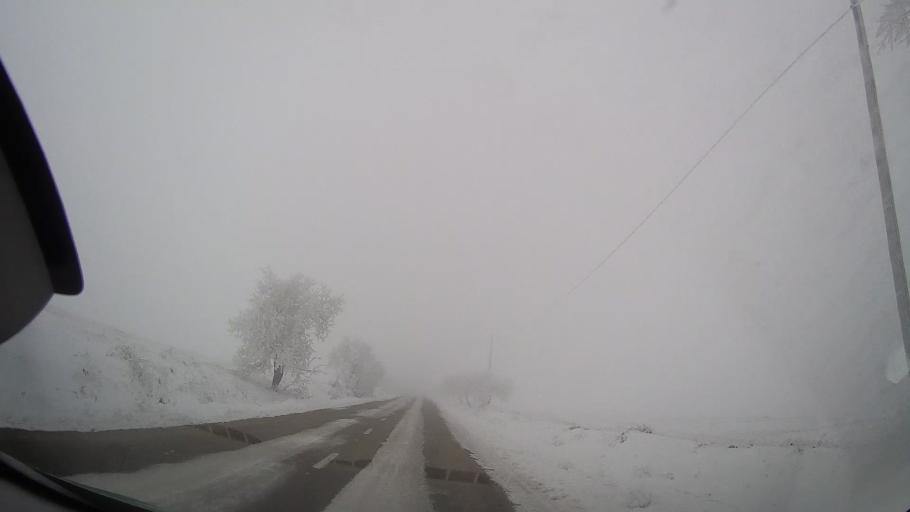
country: RO
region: Neamt
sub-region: Comuna Valea Ursului
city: Valea Ursului
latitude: 46.8022
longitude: 27.0740
